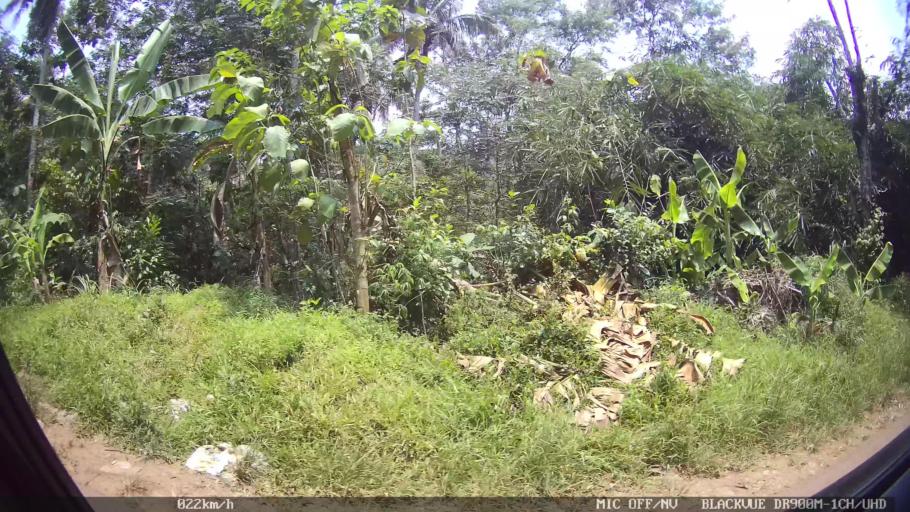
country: ID
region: Lampung
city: Pringsewu
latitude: -5.3831
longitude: 105.0103
